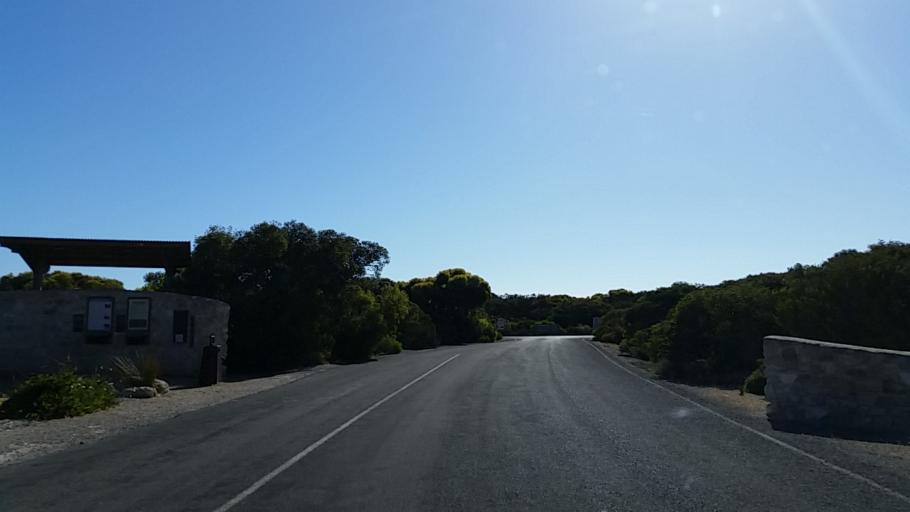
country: AU
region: South Australia
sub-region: Yorke Peninsula
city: Honiton
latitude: -35.2703
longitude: 136.9419
